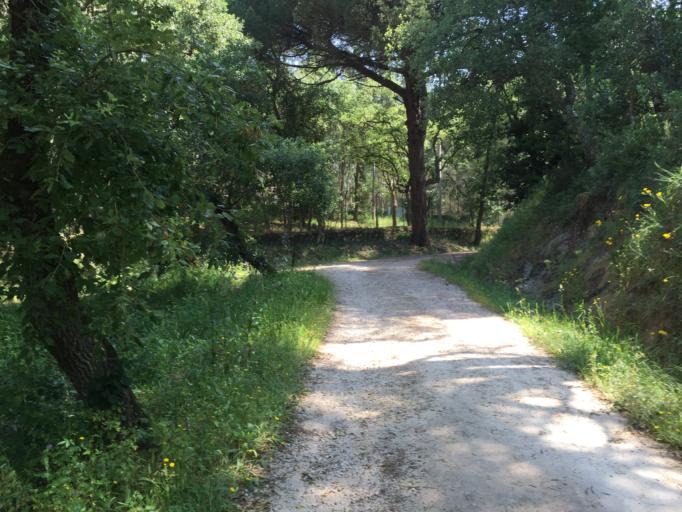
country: PT
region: Lisbon
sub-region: Mafra
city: Milharado
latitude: 38.9063
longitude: -9.1867
